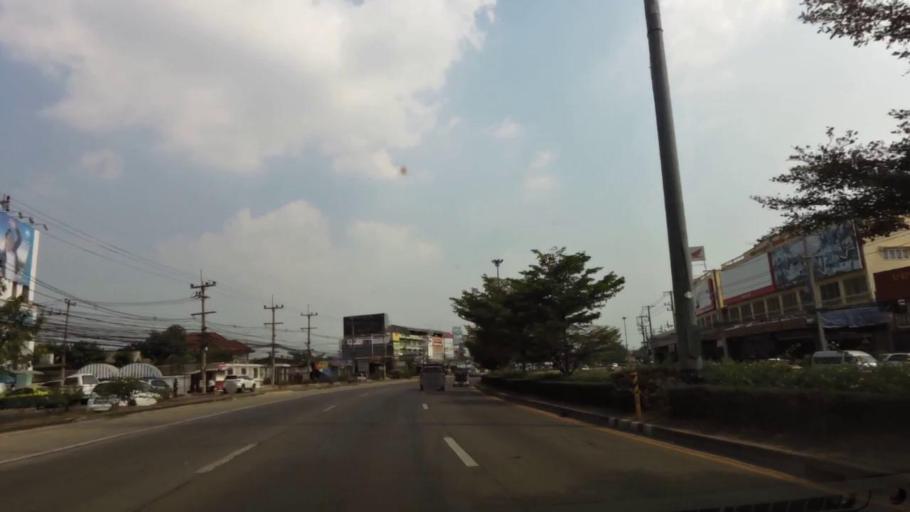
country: TH
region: Phra Nakhon Si Ayutthaya
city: Phra Nakhon Si Ayutthaya
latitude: 14.3547
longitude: 100.5983
